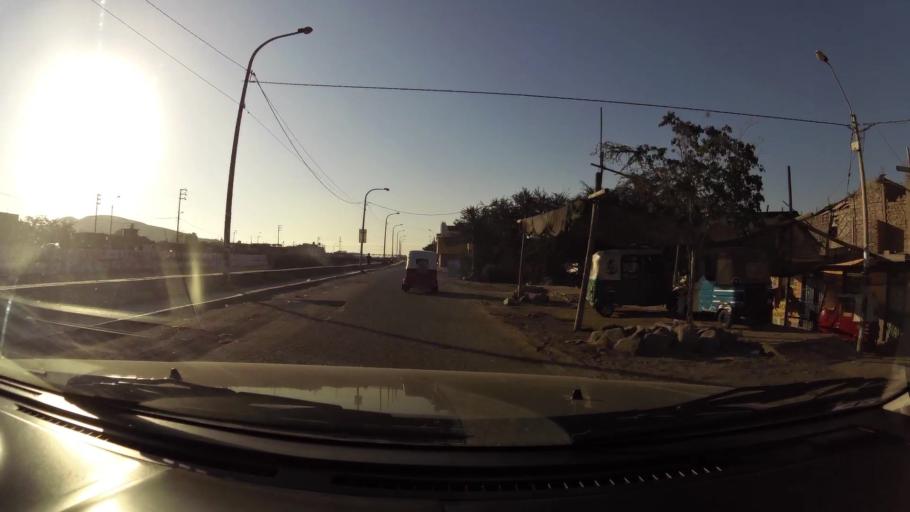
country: PE
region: Ica
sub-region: Provincia de Ica
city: Ica
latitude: -14.0574
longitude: -75.7257
